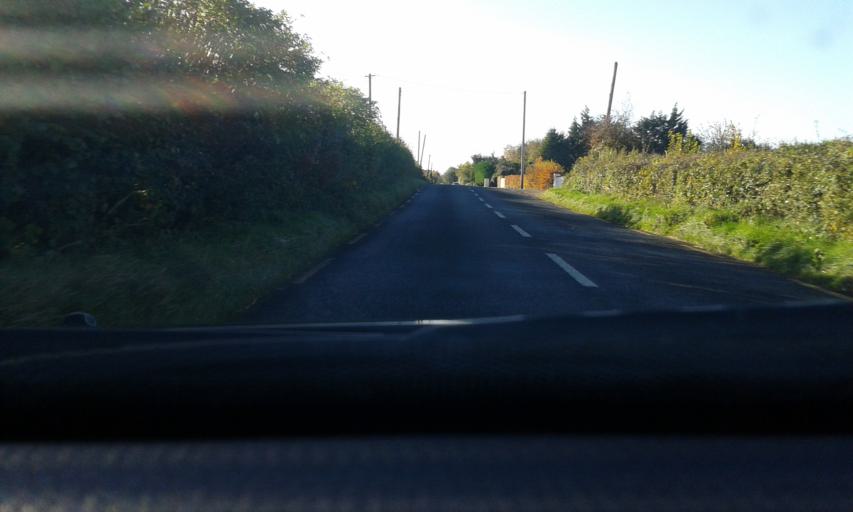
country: IE
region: Leinster
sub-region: Kildare
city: Monasterevin
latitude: 53.1703
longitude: -7.0301
